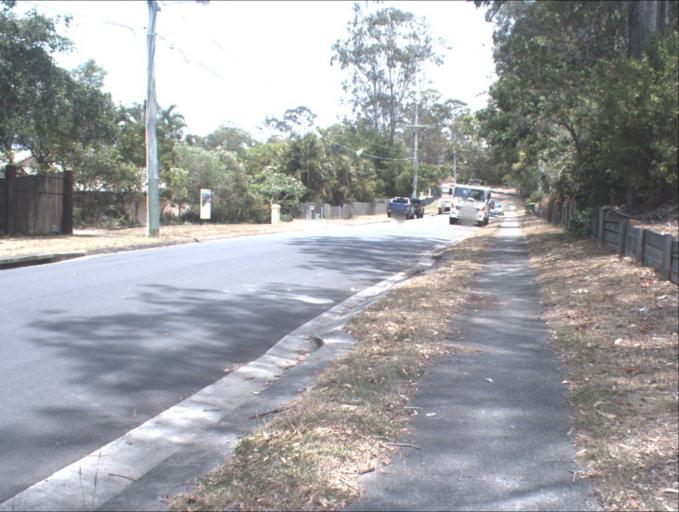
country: AU
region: Queensland
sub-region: Logan
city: Beenleigh
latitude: -27.6622
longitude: 153.1996
